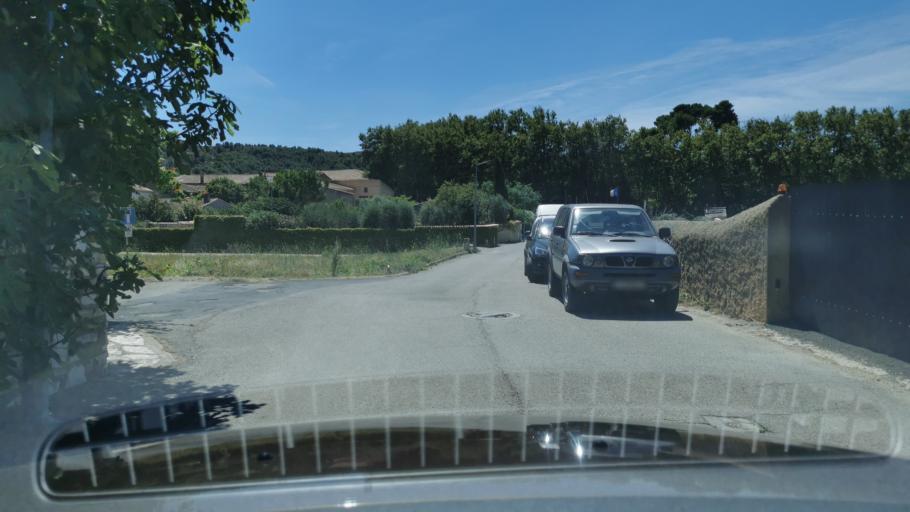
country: FR
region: Languedoc-Roussillon
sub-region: Departement de l'Aude
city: Armissan
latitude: 43.1888
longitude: 3.0945
